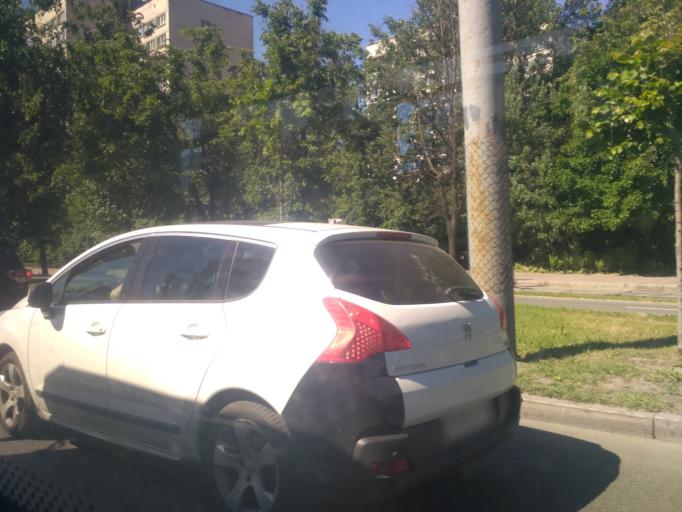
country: RU
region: Leningrad
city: Kalininskiy
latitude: 59.9719
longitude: 30.4123
